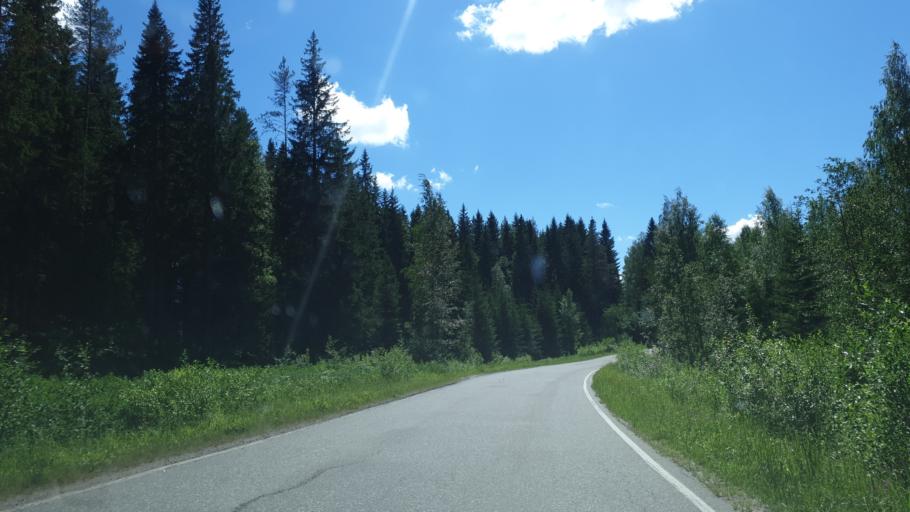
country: FI
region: Northern Savo
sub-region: Koillis-Savo
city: Kaavi
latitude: 63.0099
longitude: 28.5131
